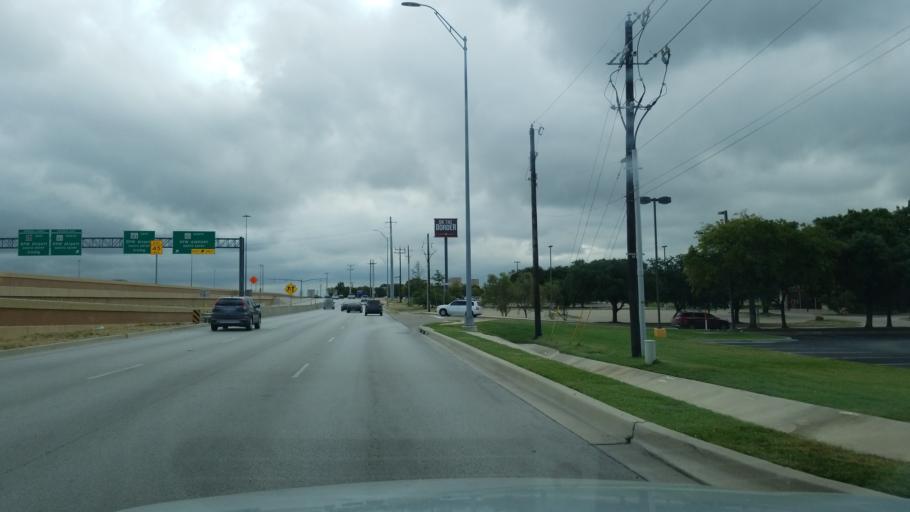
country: US
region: Texas
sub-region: Tarrant County
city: Bedford
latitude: 32.8363
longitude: -97.1299
